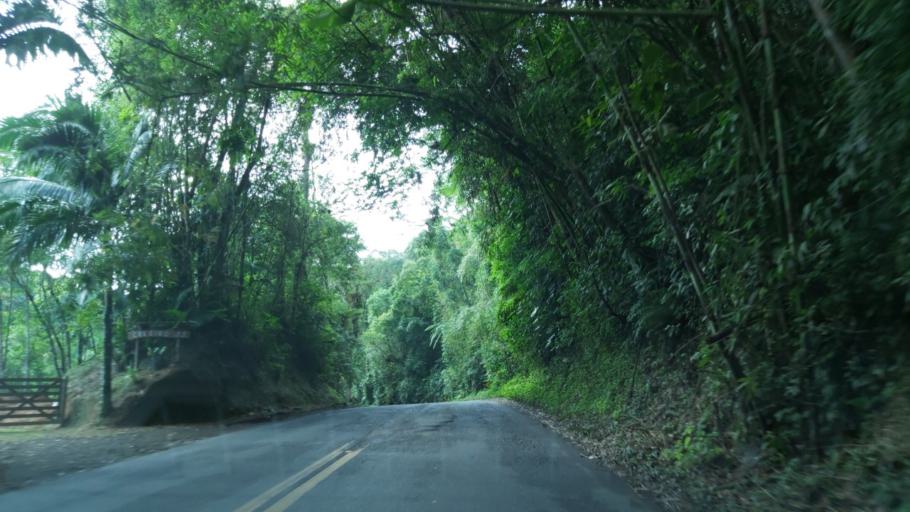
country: BR
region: Sao Paulo
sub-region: Juquia
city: Juquia
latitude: -24.0690
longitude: -47.6007
